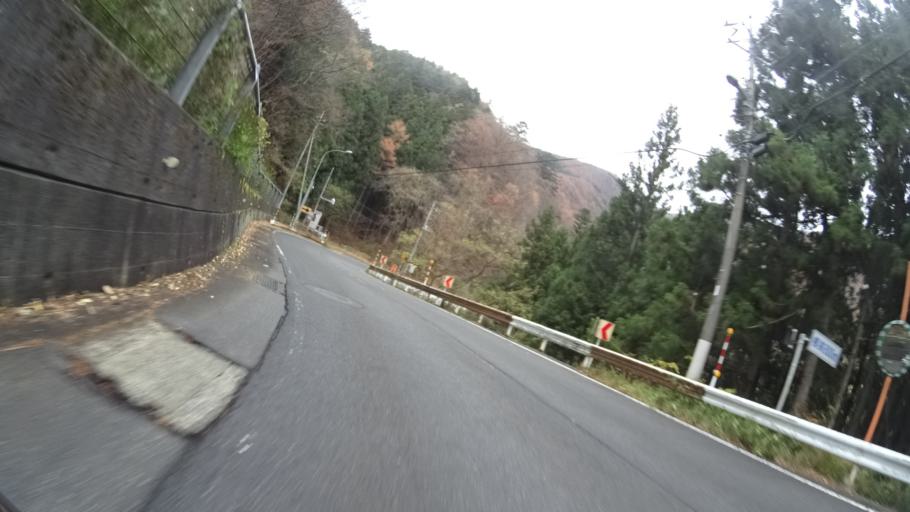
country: JP
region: Gunma
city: Nakanojomachi
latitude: 36.7327
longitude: 138.8507
